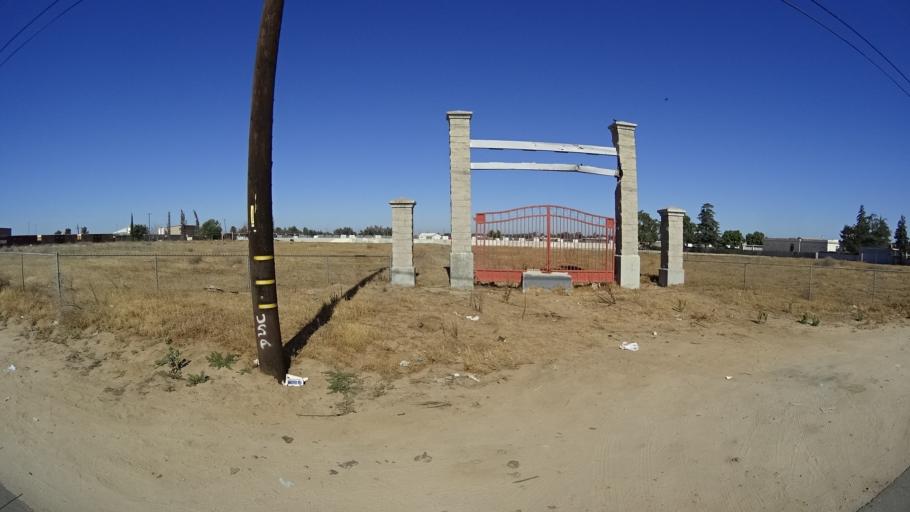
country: US
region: California
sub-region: Fresno County
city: West Park
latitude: 36.7475
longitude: -119.8355
